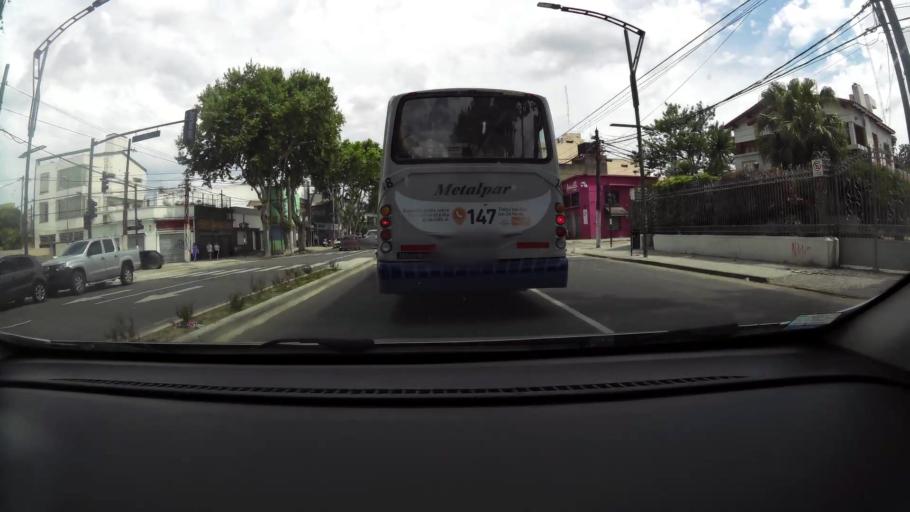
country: AR
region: Santa Fe
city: Gobernador Galvez
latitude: -32.9947
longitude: -60.6476
